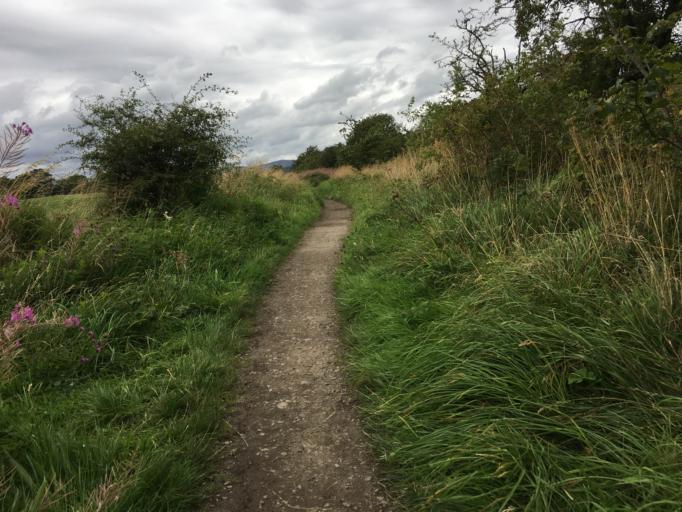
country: GB
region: Scotland
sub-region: Stirling
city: Killearn
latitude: 56.0464
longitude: -4.4000
